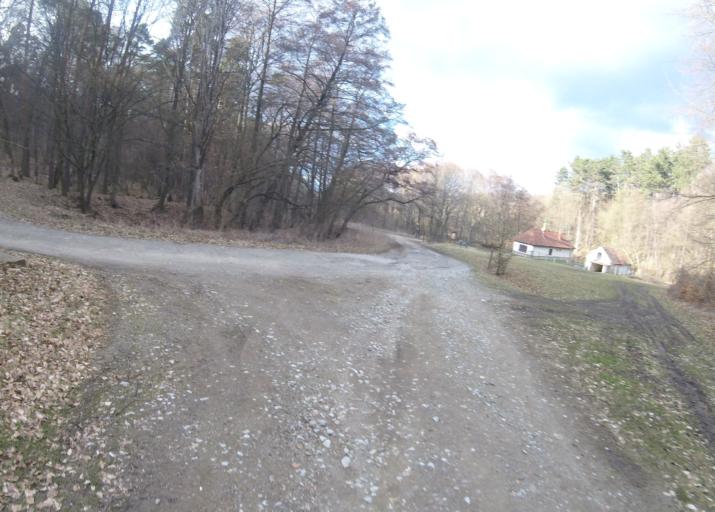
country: HU
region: Heves
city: Belapatfalva
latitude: 48.0366
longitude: 20.3533
